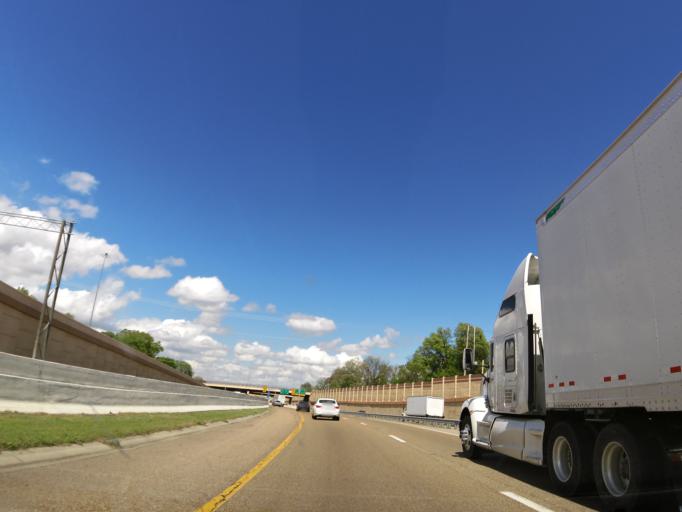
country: US
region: Tennessee
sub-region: Shelby County
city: Memphis
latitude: 35.1515
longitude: -90.0216
